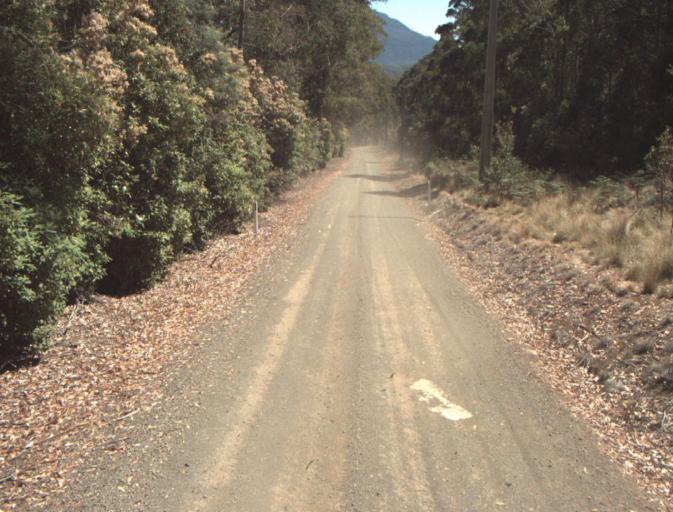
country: AU
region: Tasmania
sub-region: Dorset
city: Scottsdale
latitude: -41.3553
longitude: 147.3917
